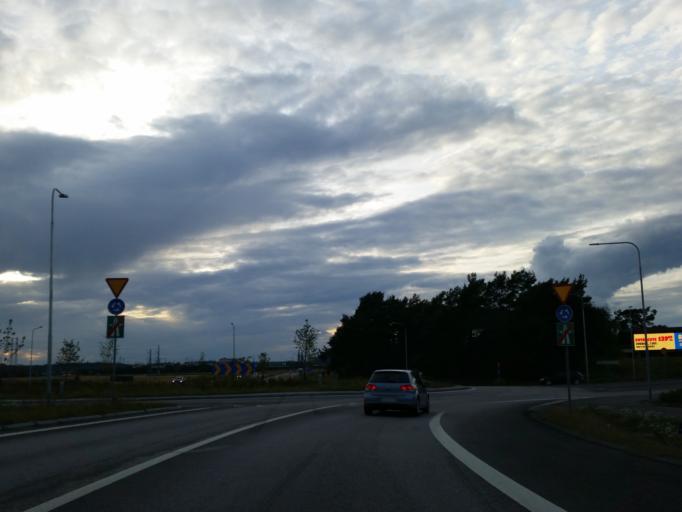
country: SE
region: Uppsala
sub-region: Uppsala Kommun
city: Saevja
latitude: 59.8428
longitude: 17.7117
